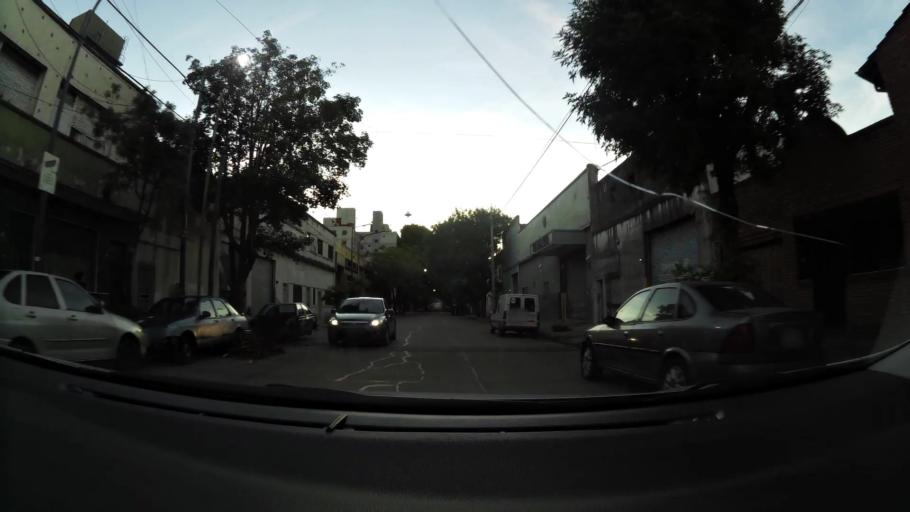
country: AR
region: Buenos Aires F.D.
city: Villa Lugano
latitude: -34.6403
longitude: -58.4375
